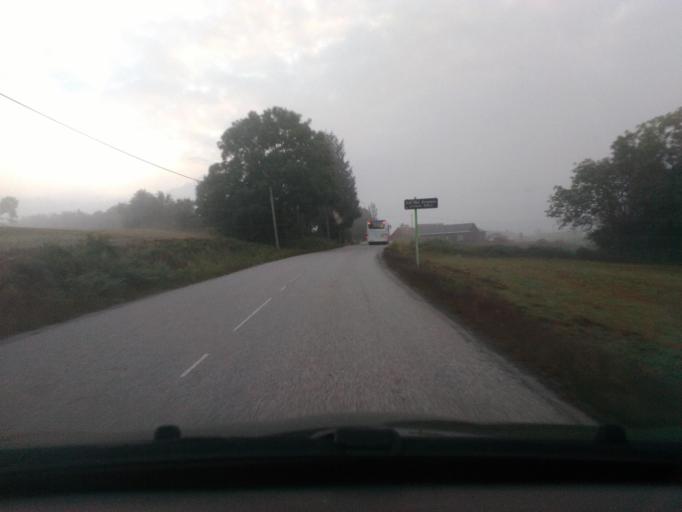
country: FR
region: Lorraine
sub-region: Departement des Vosges
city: Corcieux
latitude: 48.1475
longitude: 6.8616
